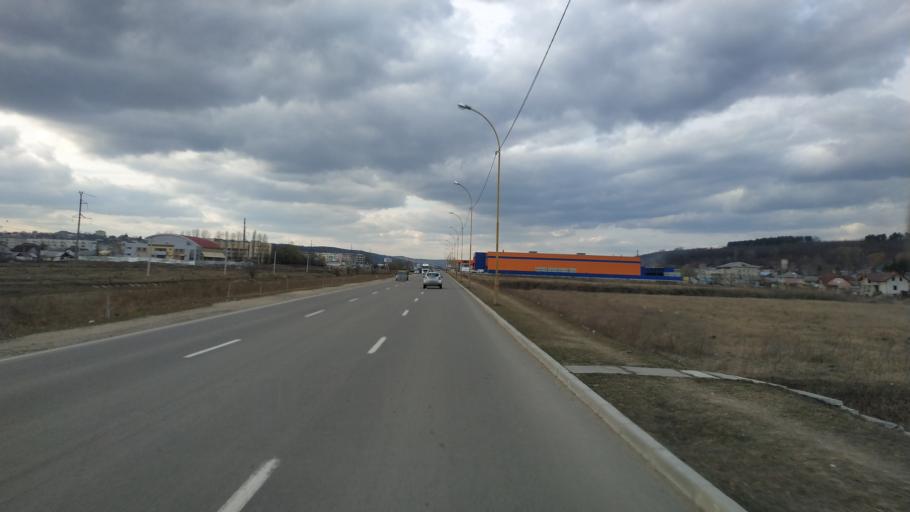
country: MD
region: Hincesti
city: Hincesti
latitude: 46.8274
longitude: 28.6027
